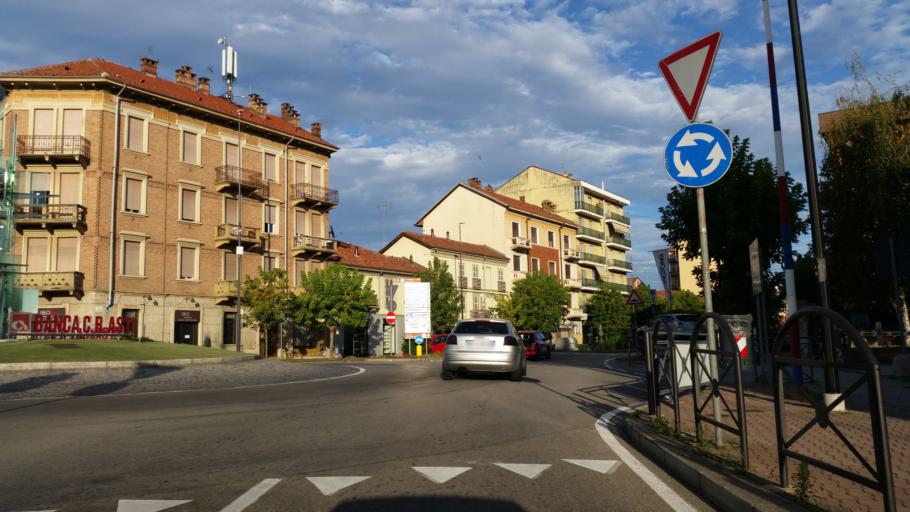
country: IT
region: Piedmont
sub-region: Provincia di Asti
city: Asti
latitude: 44.9059
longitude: 8.1854
